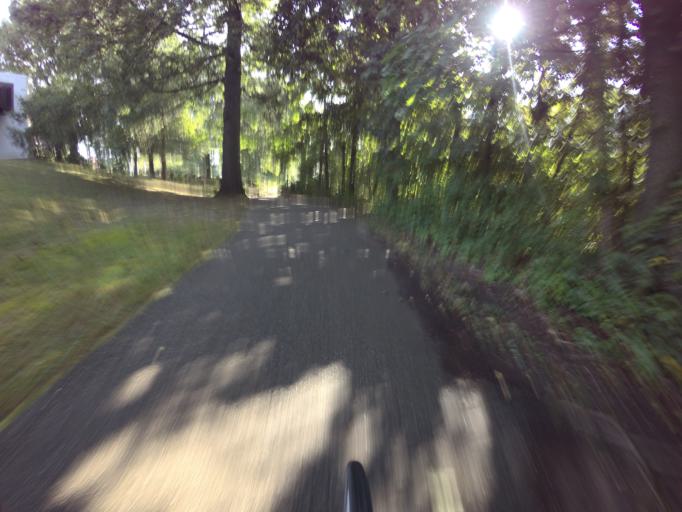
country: US
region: Maryland
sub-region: Anne Arundel County
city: Glen Burnie
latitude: 39.1676
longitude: -76.6353
